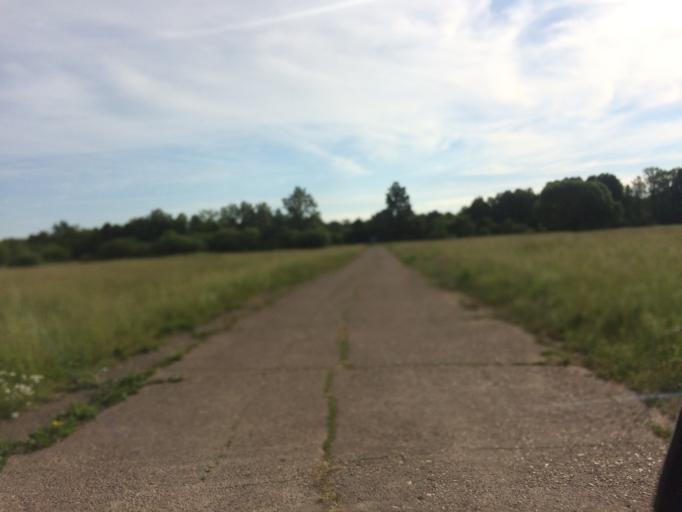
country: RU
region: Mariy-El
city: Yoshkar-Ola
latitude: 56.6557
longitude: 47.9230
